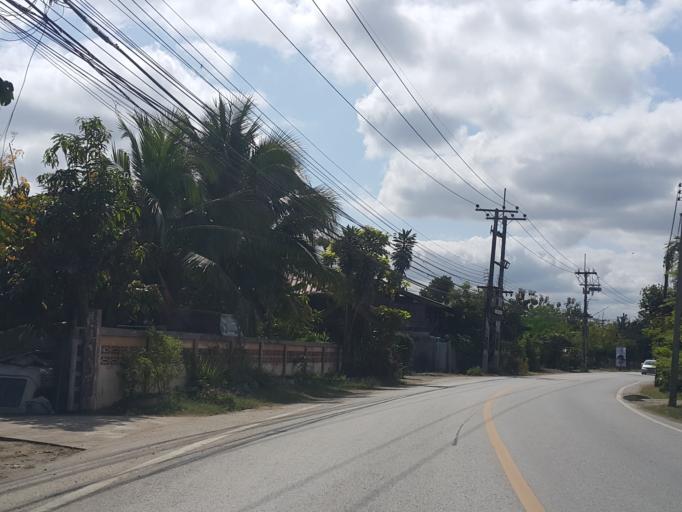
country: TH
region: Lamphun
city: Ban Thi
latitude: 18.6679
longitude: 99.1360
